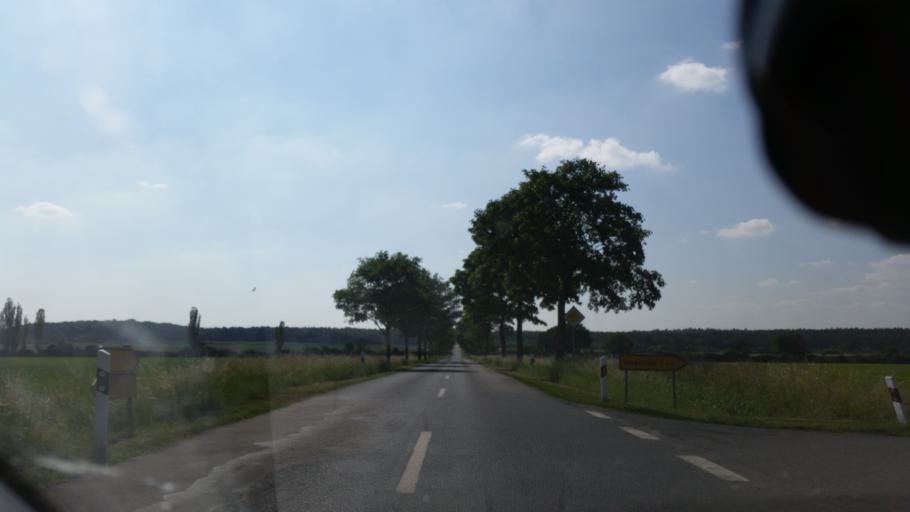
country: DE
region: Lower Saxony
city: Lehre
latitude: 52.3146
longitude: 10.7429
